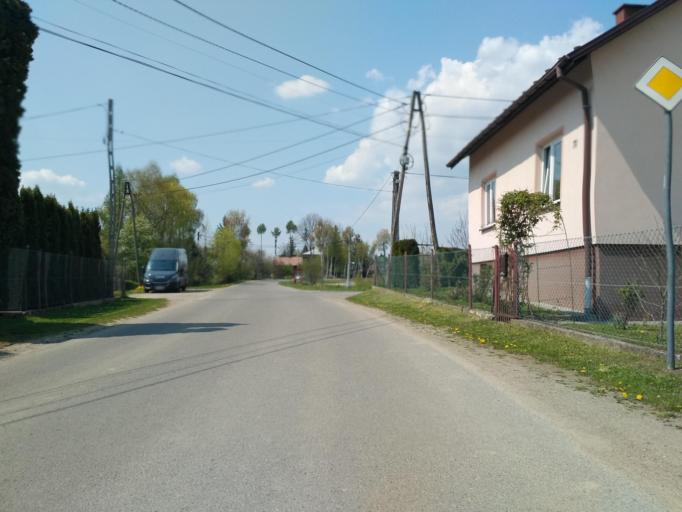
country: PL
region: Subcarpathian Voivodeship
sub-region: Powiat jasielski
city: Jaslo
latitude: 49.7105
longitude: 21.5094
